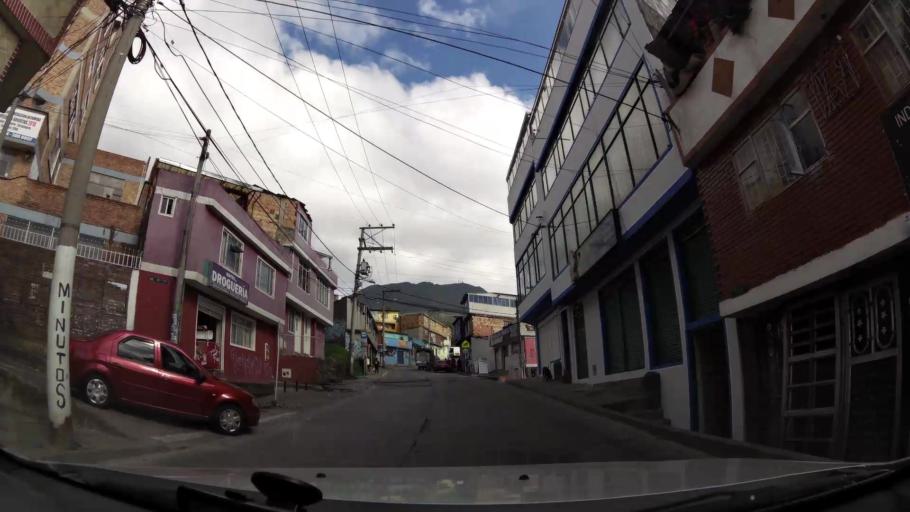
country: CO
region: Bogota D.C.
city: Bogota
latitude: 4.5433
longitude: -74.0881
